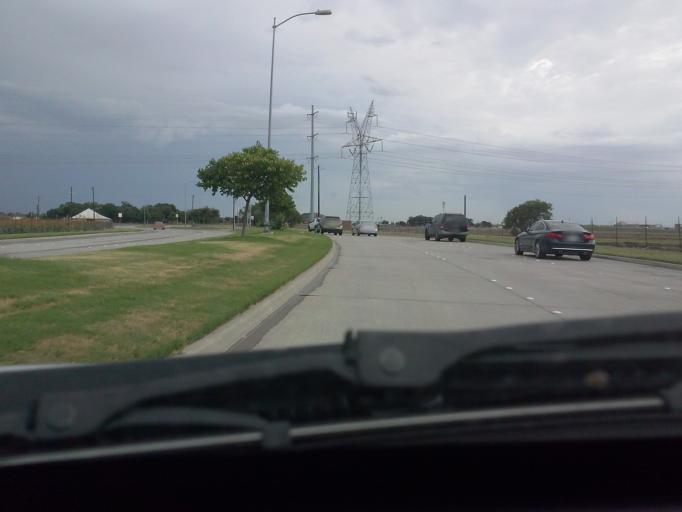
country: US
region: Texas
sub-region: Denton County
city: The Colony
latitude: 33.0617
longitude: -96.8229
